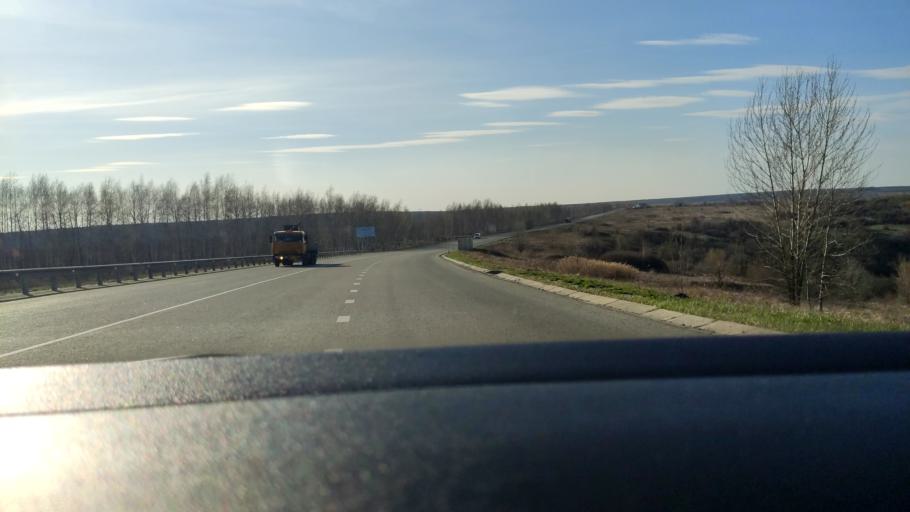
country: RU
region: Voronezj
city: Kolodeznyy
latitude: 51.3226
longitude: 39.1107
